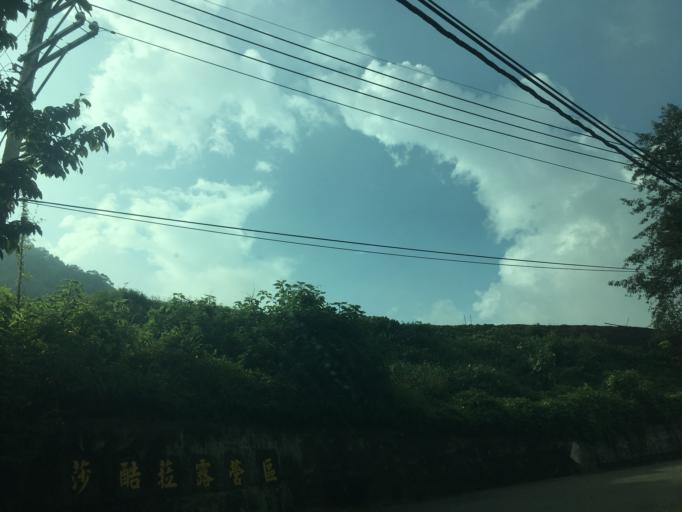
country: TW
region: Taiwan
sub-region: Miaoli
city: Miaoli
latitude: 24.4034
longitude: 120.9766
